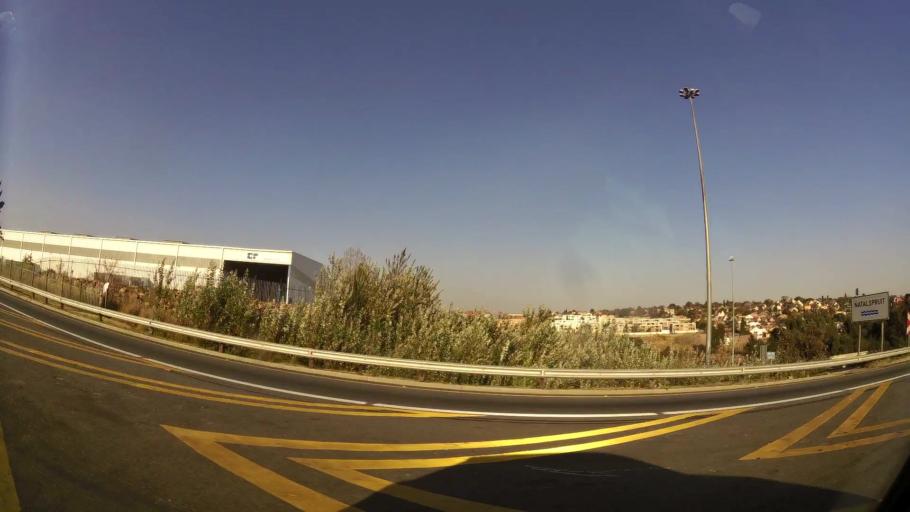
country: ZA
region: Gauteng
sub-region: Ekurhuleni Metropolitan Municipality
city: Germiston
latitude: -26.2442
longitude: 28.1249
